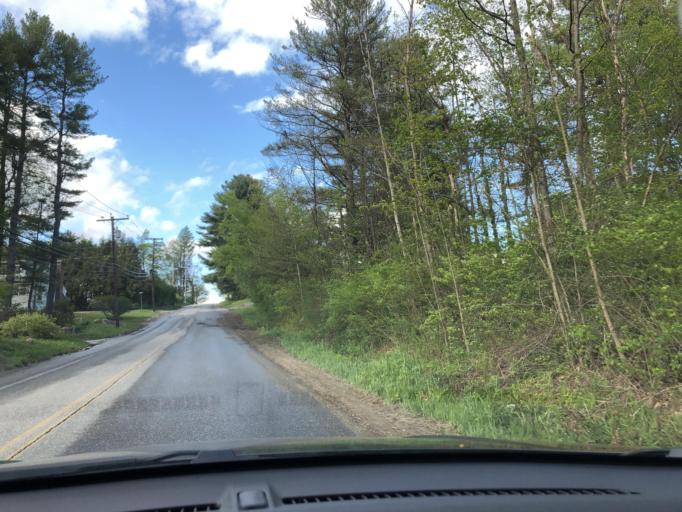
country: US
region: New Hampshire
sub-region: Merrimack County
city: New London
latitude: 43.4123
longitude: -71.9866
